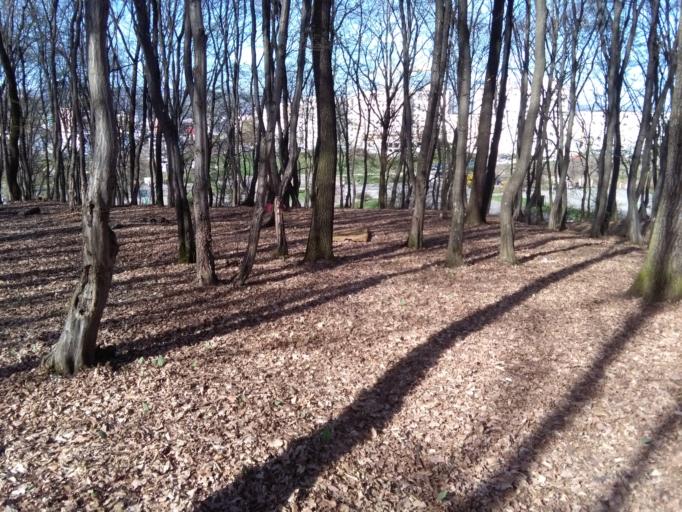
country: RO
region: Cluj
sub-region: Municipiul Cluj-Napoca
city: Cluj-Napoca
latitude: 46.7479
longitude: 23.5543
